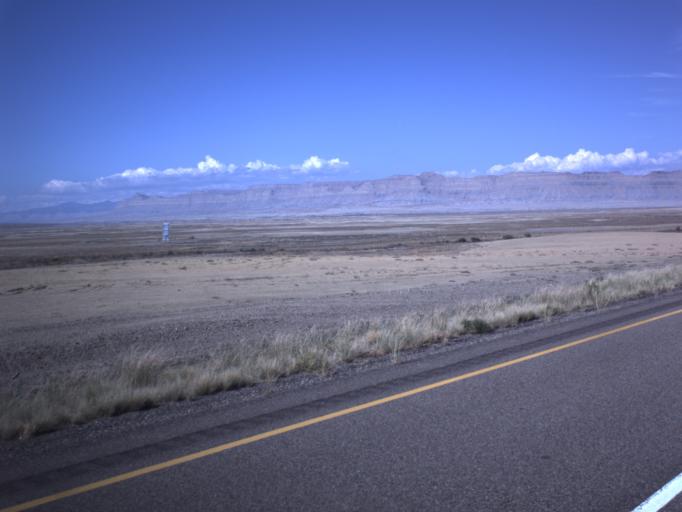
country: US
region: Utah
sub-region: Carbon County
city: East Carbon City
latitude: 38.9457
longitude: -110.3246
